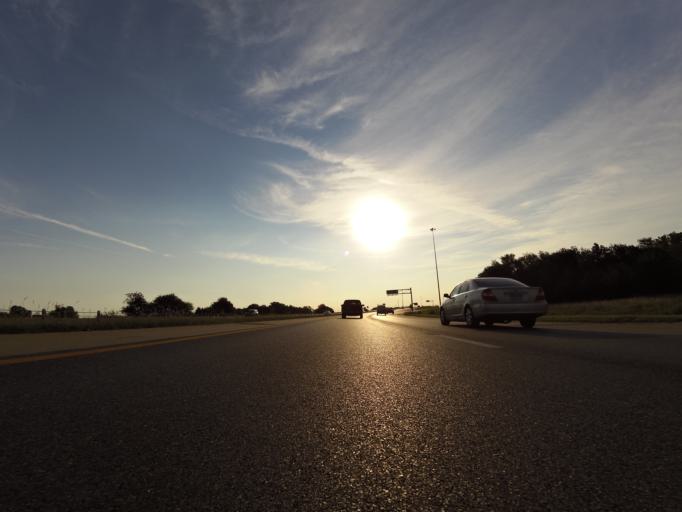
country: US
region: Kansas
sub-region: Sedgwick County
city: Bellaire
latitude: 37.7452
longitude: -97.2860
